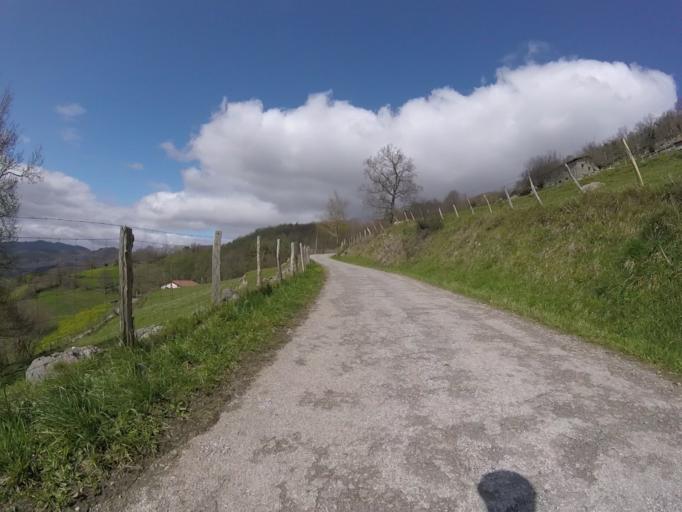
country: ES
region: Basque Country
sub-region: Provincia de Guipuzcoa
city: Albiztur
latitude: 43.1387
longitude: -2.1133
